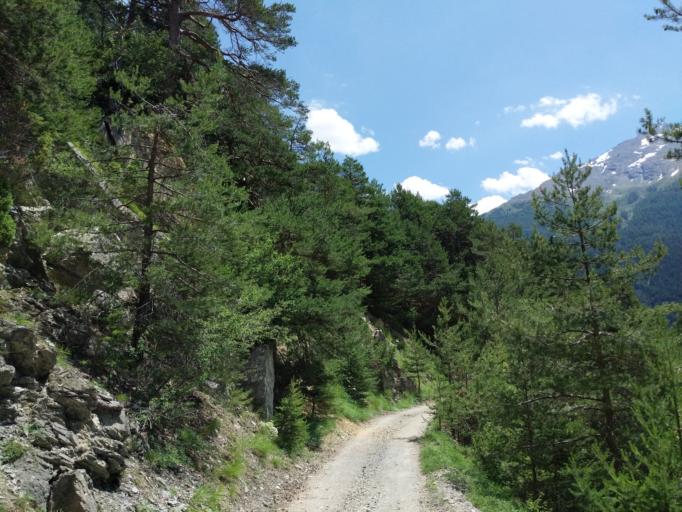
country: FR
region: Rhone-Alpes
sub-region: Departement de la Savoie
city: Modane
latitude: 45.2245
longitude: 6.7493
